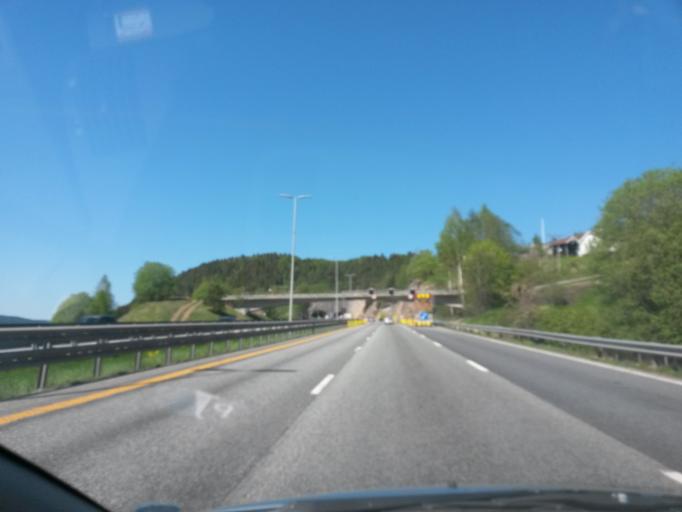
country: NO
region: Buskerud
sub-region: Lier
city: Tranby
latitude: 59.7870
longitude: 10.2731
